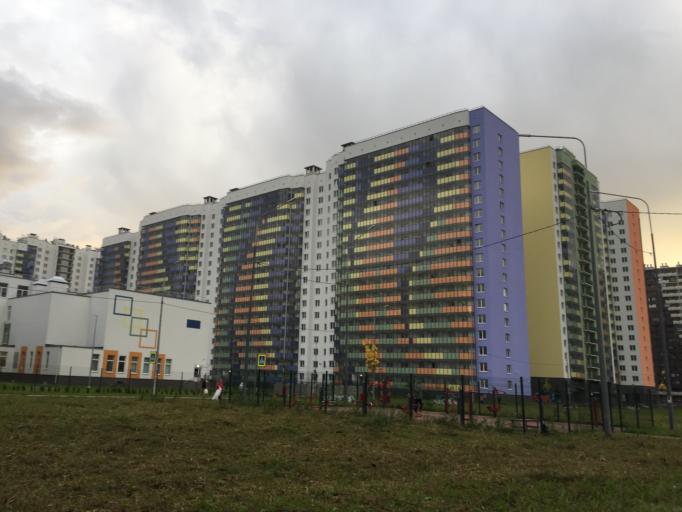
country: RU
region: Leningrad
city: Murino
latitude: 60.0580
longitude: 30.4453
